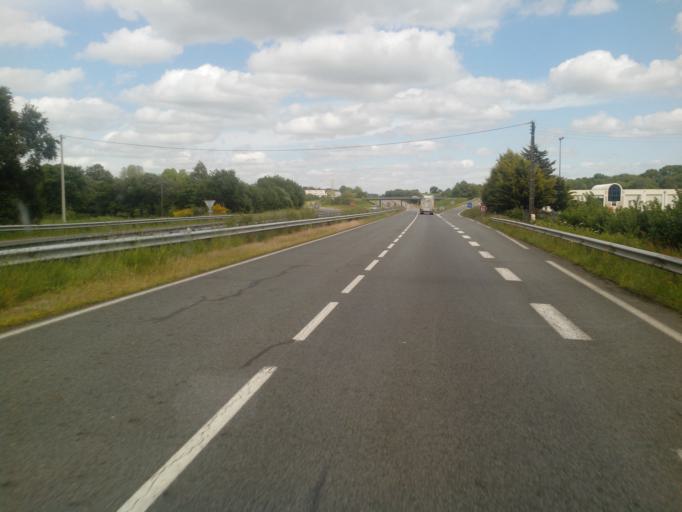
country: FR
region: Brittany
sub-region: Departement des Cotes-d'Armor
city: Belle-Isle-en-Terre
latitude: 48.5524
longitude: -3.3773
